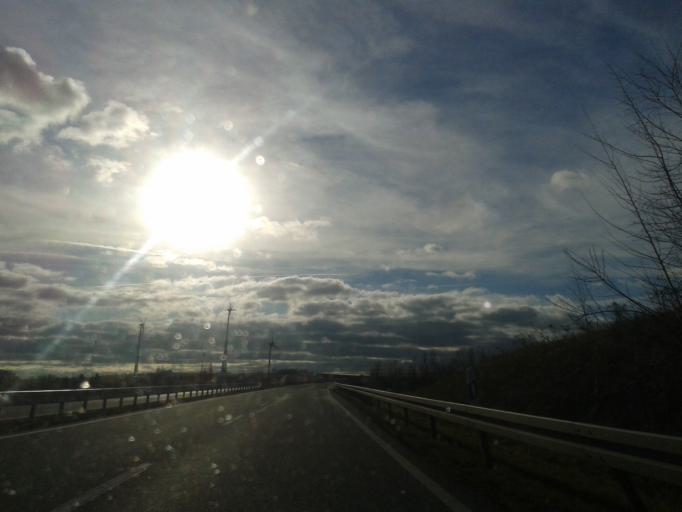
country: DE
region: Saxony
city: Lobau
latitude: 51.1408
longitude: 14.6538
